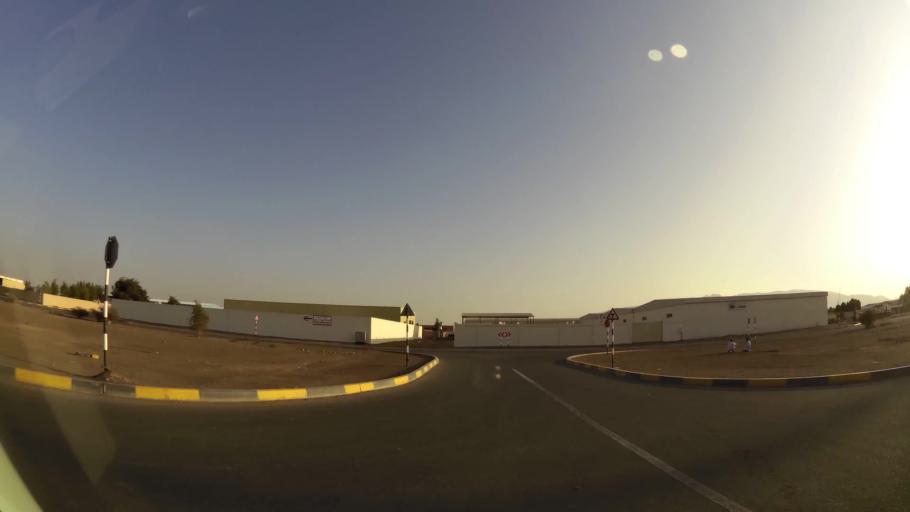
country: AE
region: Abu Dhabi
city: Al Ain
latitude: 24.1508
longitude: 55.8302
